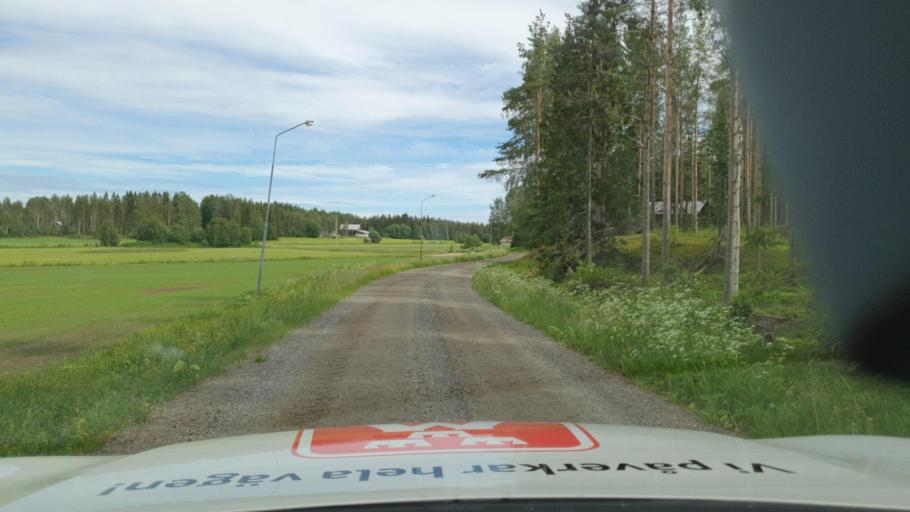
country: SE
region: Vaesterbotten
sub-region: Robertsfors Kommun
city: Robertsfors
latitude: 64.3740
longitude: 21.0413
